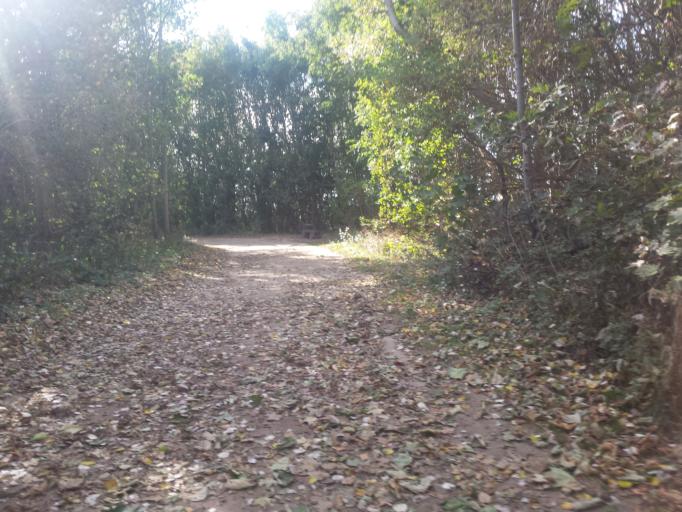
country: DE
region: Mecklenburg-Vorpommern
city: Altenkirchen
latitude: 54.6744
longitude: 13.4333
